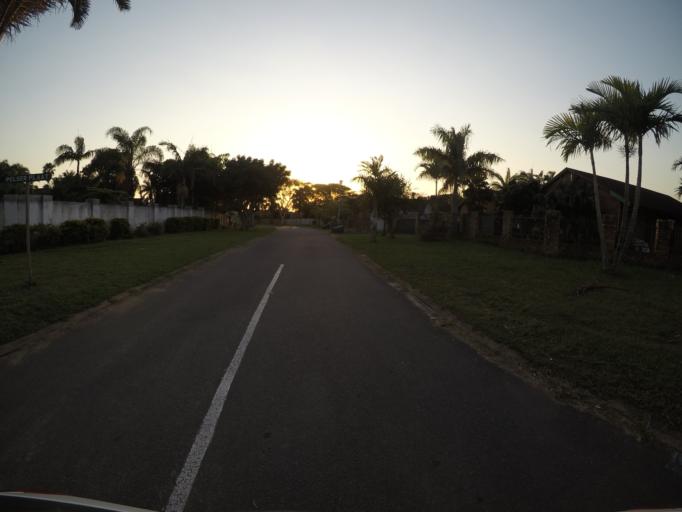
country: ZA
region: KwaZulu-Natal
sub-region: uThungulu District Municipality
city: Richards Bay
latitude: -28.7671
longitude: 32.1175
